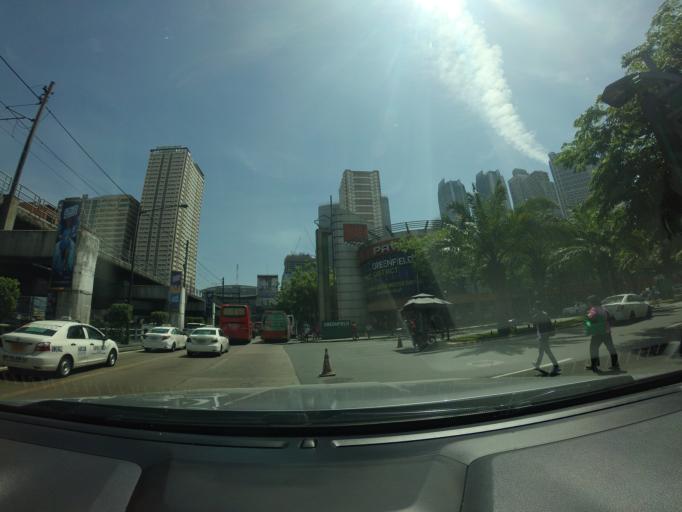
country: PH
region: Metro Manila
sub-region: Pasig
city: Pasig City
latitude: 14.5791
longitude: 121.0525
